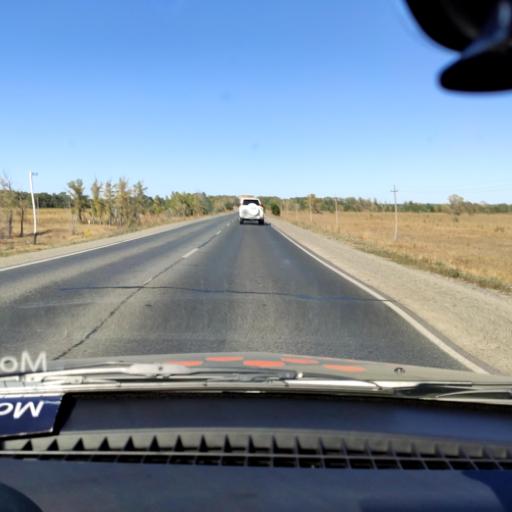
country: RU
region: Orenburg
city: Tatarskaya Kargala
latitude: 51.9207
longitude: 55.1739
